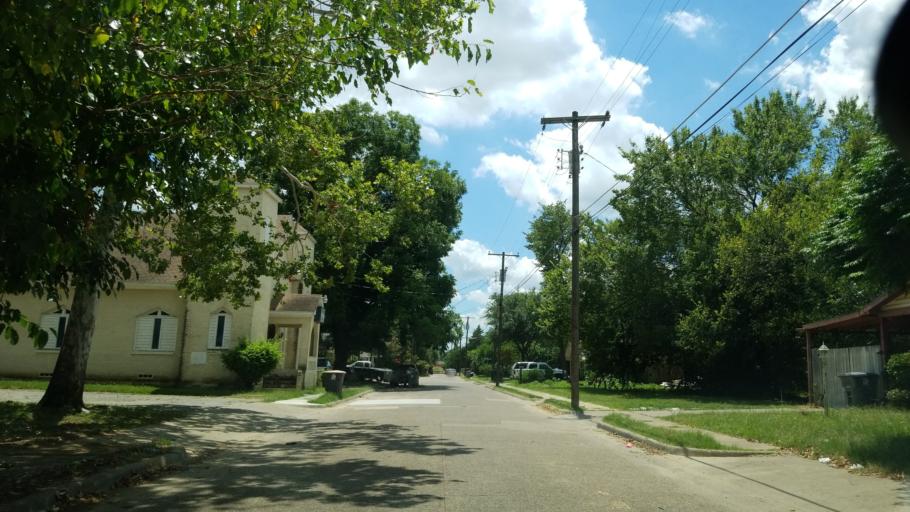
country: US
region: Texas
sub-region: Dallas County
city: Dallas
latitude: 32.7434
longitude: -96.7552
